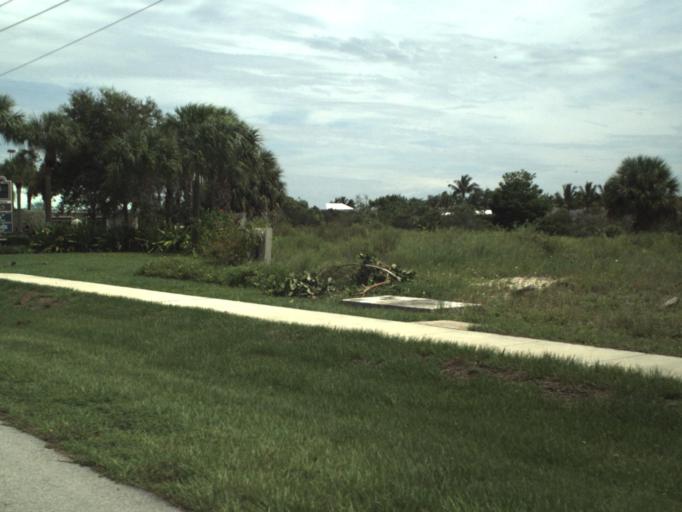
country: US
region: Florida
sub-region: Palm Beach County
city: Jupiter
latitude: 26.9118
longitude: -80.0698
